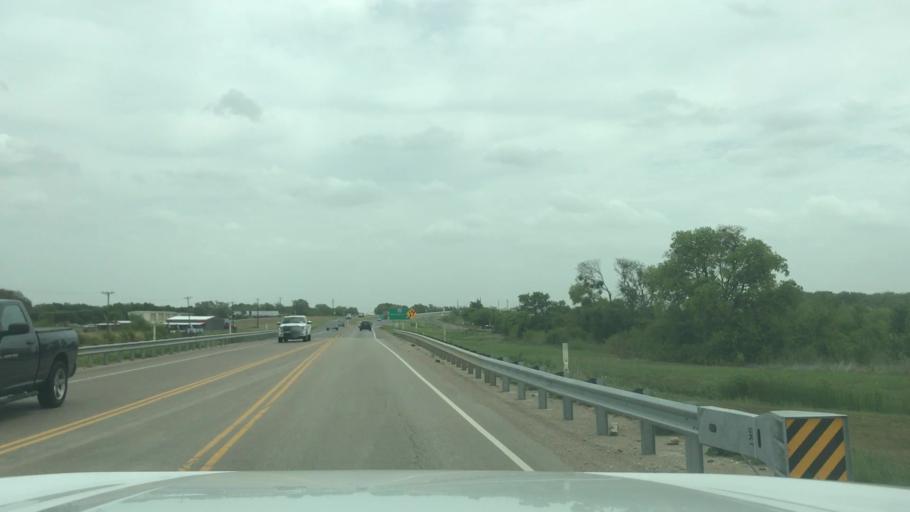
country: US
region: Texas
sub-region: McLennan County
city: Woodway
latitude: 31.5775
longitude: -97.2958
